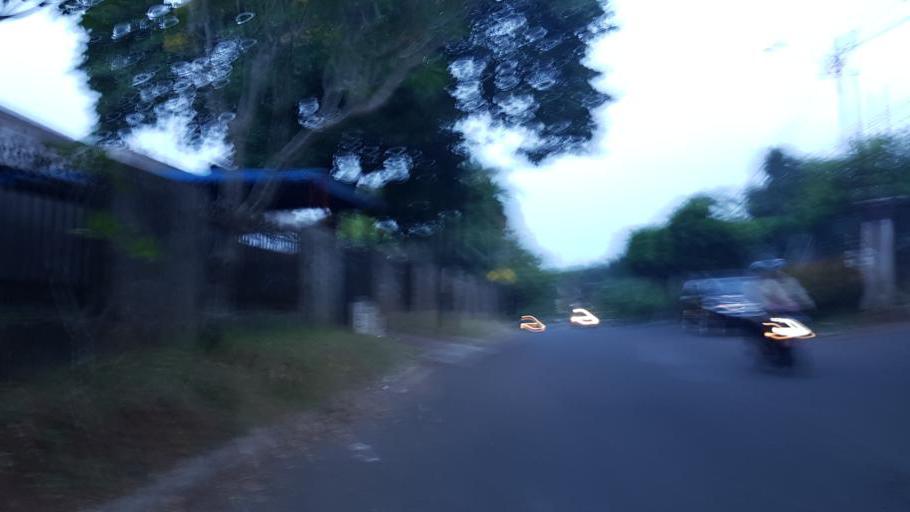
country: ID
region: West Java
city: Pamulang
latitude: -6.3196
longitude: 106.7865
